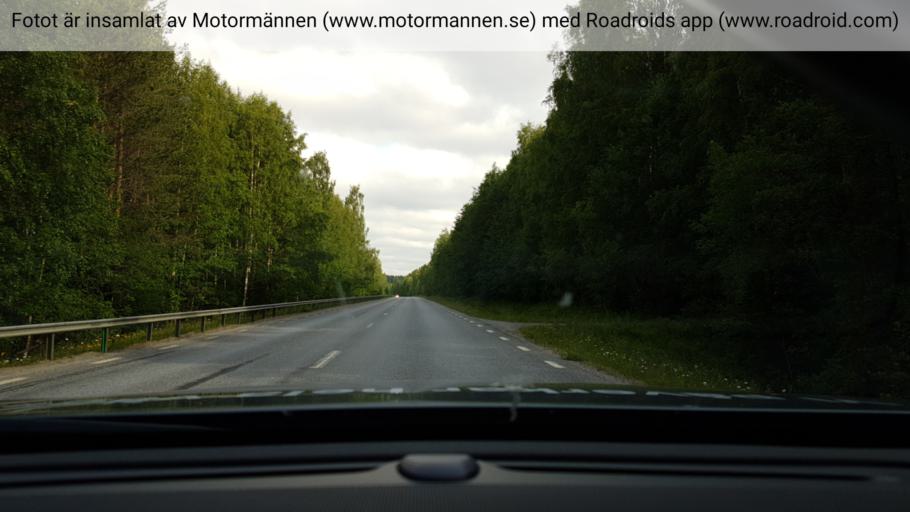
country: SE
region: Vaesterbotten
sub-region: Vindelns Kommun
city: Vindeln
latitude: 64.3011
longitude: 19.6163
